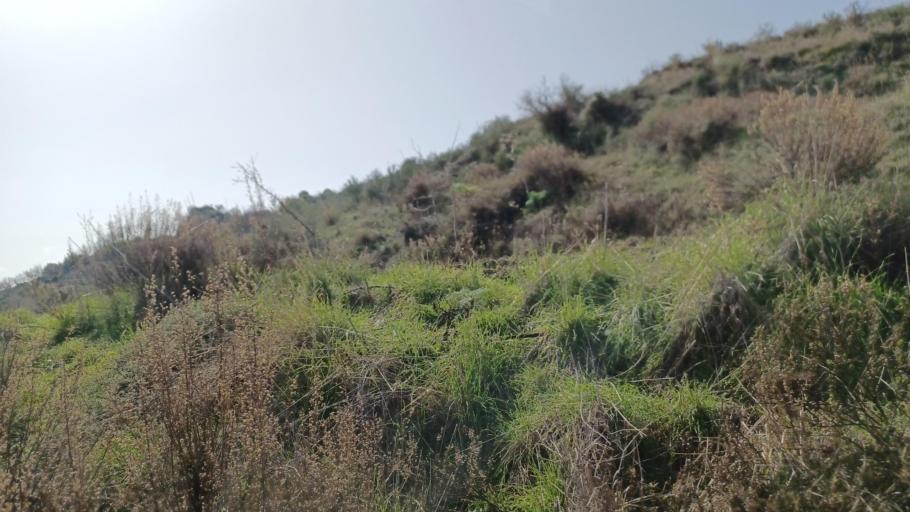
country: CY
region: Limassol
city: Pachna
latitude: 34.8024
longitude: 32.6922
